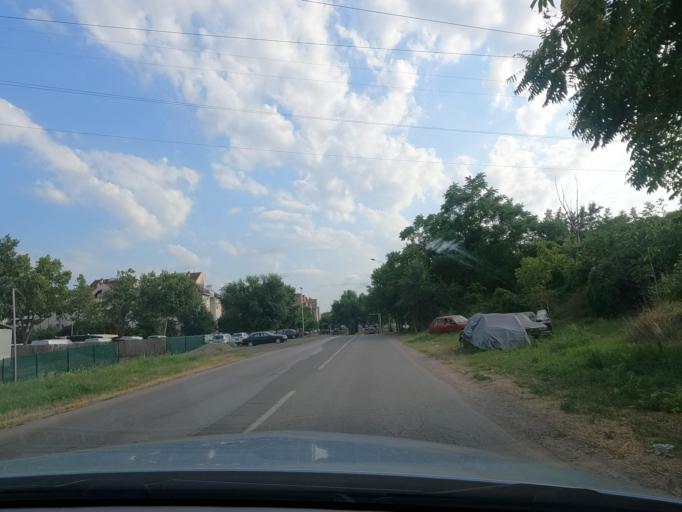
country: RS
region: Central Serbia
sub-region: Belgrade
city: Zemun
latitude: 44.8212
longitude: 20.3793
